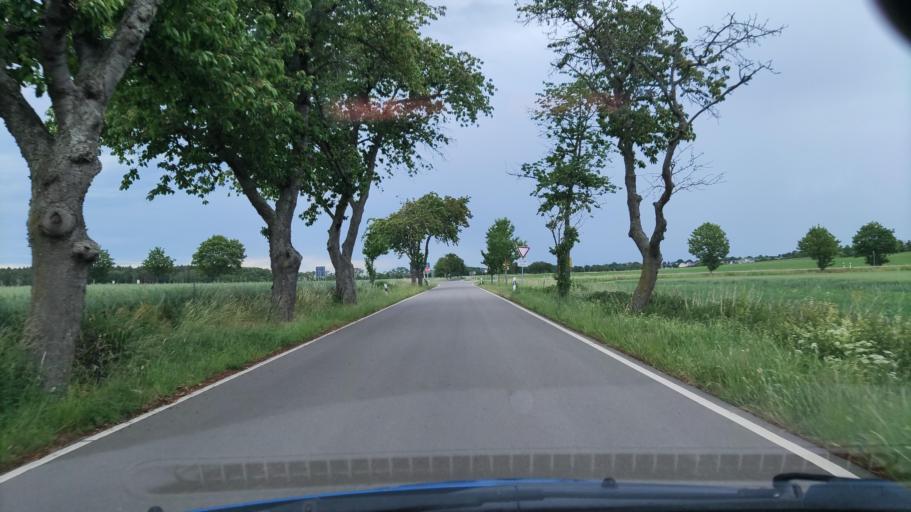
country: DE
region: Saxony-Anhalt
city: Kalbe
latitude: 52.6136
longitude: 11.3185
